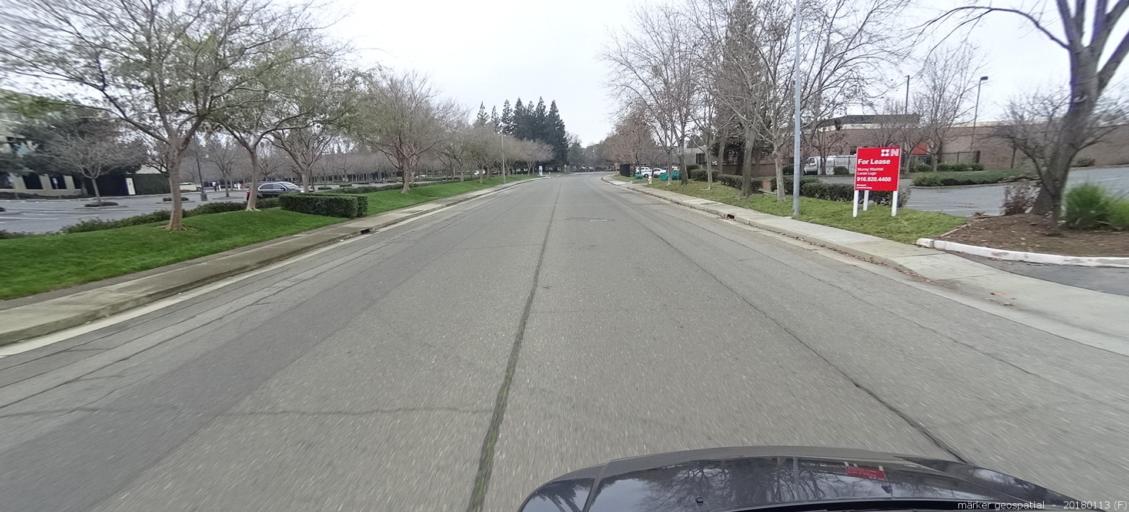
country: US
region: California
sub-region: Sacramento County
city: Rancho Cordova
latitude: 38.5910
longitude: -121.2820
